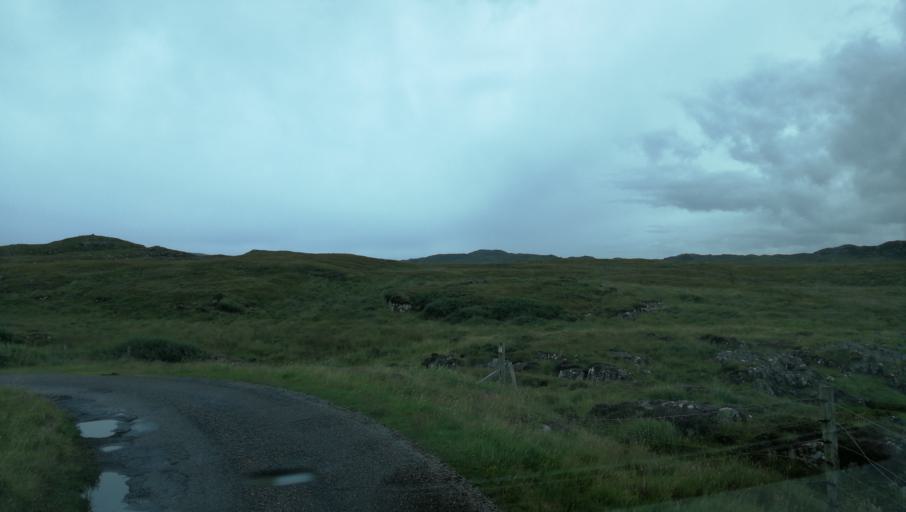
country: GB
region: Scotland
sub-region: Argyll and Bute
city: Isle Of Mull
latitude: 56.7223
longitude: -6.2191
